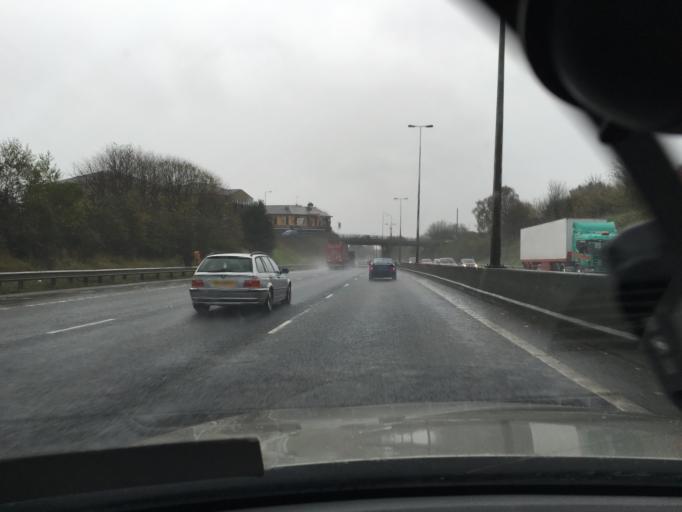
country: GB
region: Northern Ireland
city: Carnmoney
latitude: 54.6649
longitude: -5.9503
